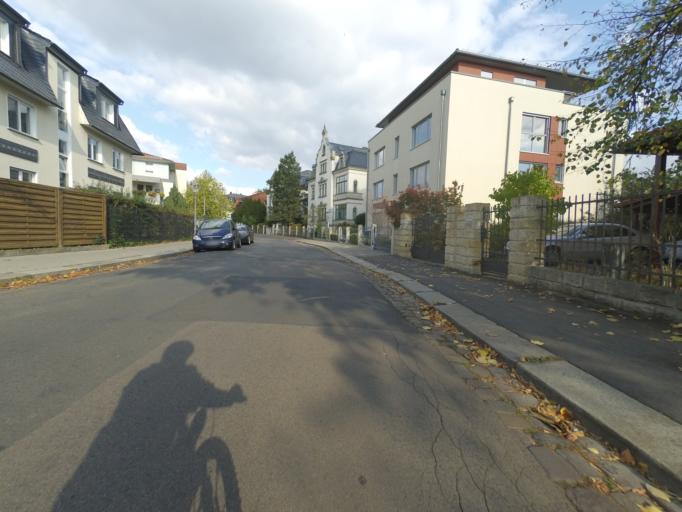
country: DE
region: Saxony
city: Albertstadt
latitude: 51.0519
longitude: 13.7872
